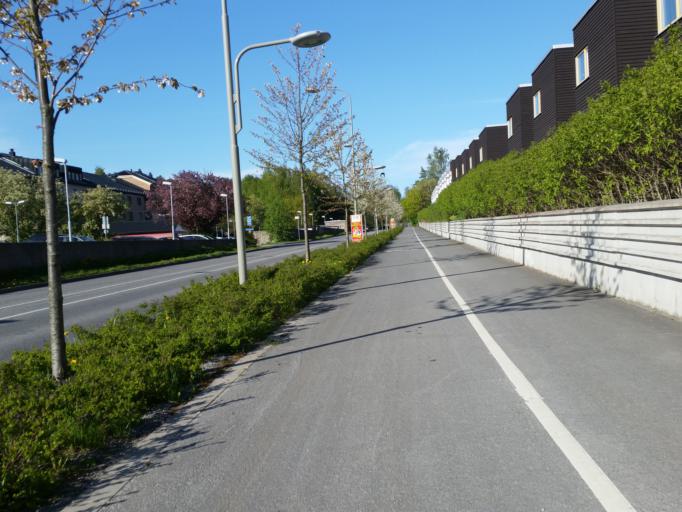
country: SE
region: Stockholm
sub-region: Stockholms Kommun
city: Arsta
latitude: 59.2848
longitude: 18.0990
